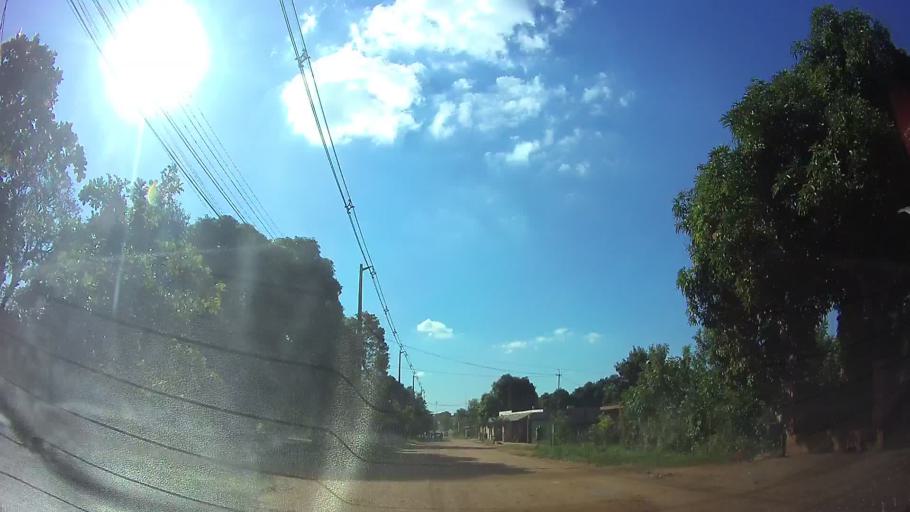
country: PY
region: Central
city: Limpio
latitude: -25.2423
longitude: -57.4744
